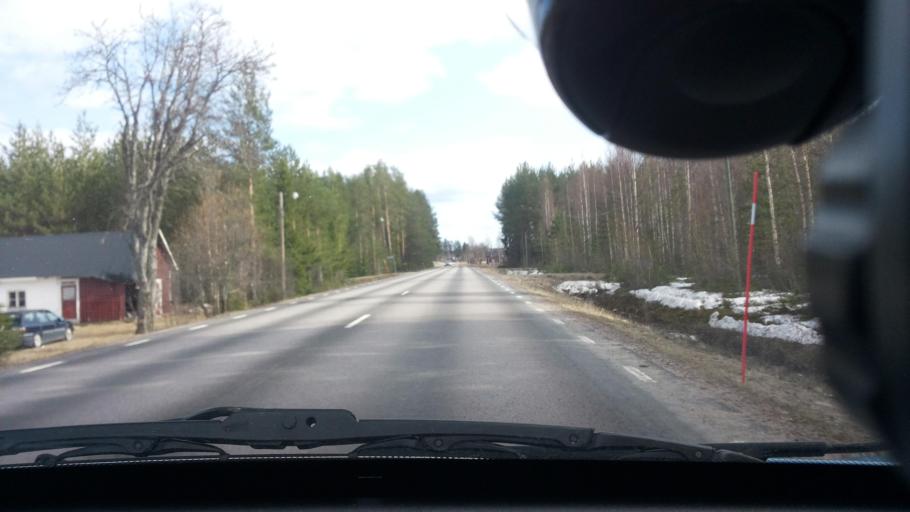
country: SE
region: Norrbotten
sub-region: Lulea Kommun
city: Sodra Sunderbyn
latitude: 65.6477
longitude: 21.8794
